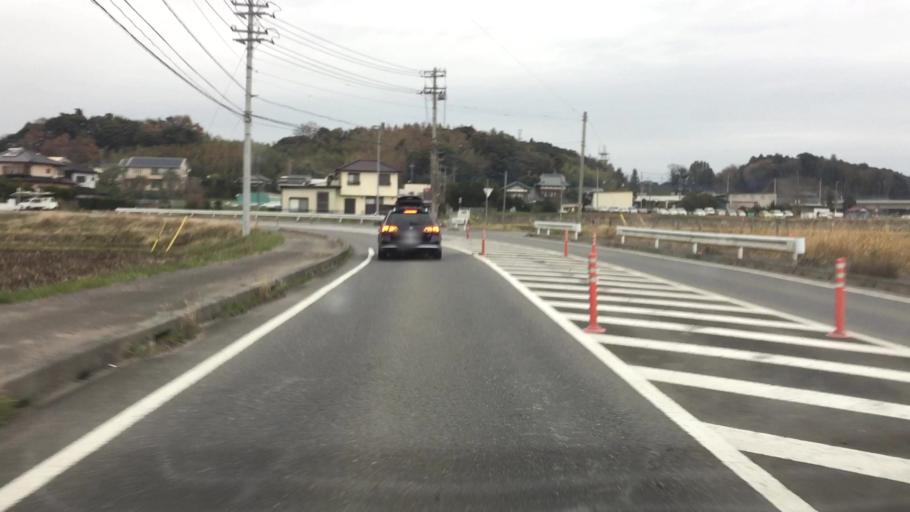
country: JP
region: Ibaraki
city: Edosaki
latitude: 35.9254
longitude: 140.3437
